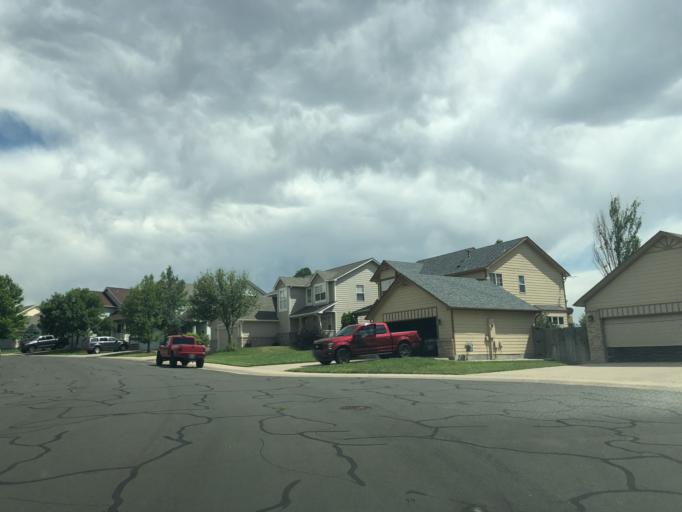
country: US
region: Colorado
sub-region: Arapahoe County
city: Dove Valley
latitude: 39.6206
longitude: -104.7712
